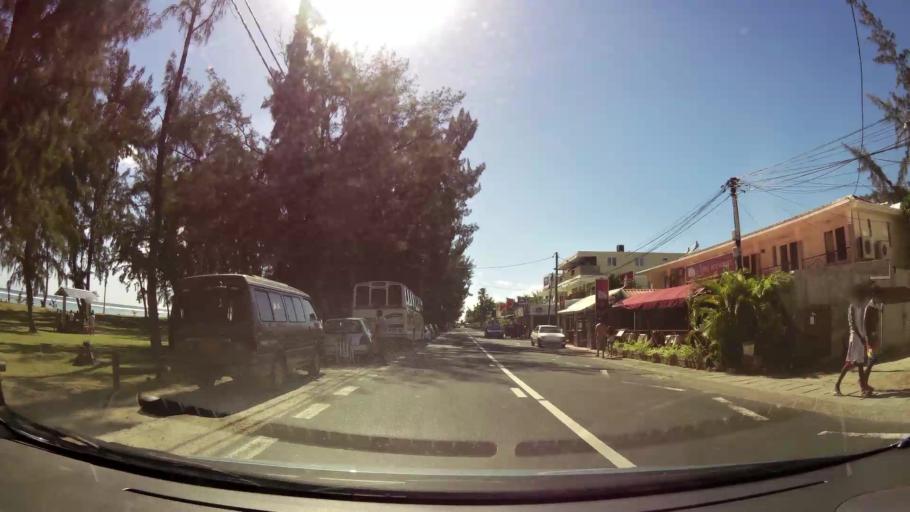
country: MU
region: Black River
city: Flic en Flac
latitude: -20.2839
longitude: 57.3646
